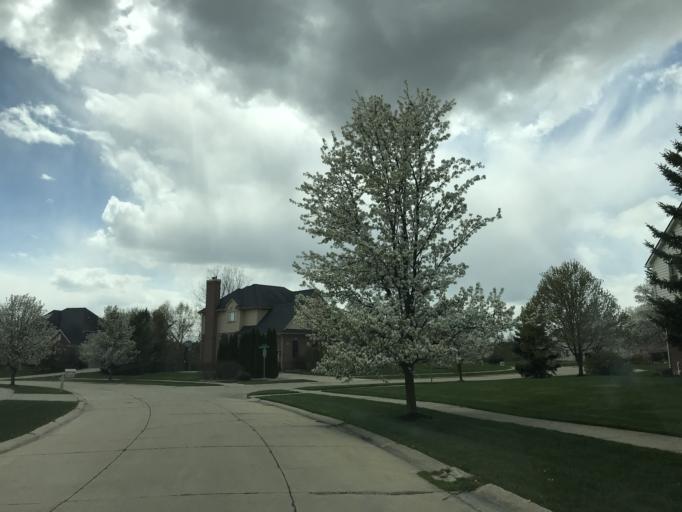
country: US
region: Michigan
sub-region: Wayne County
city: Plymouth
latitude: 42.3797
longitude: -83.5261
